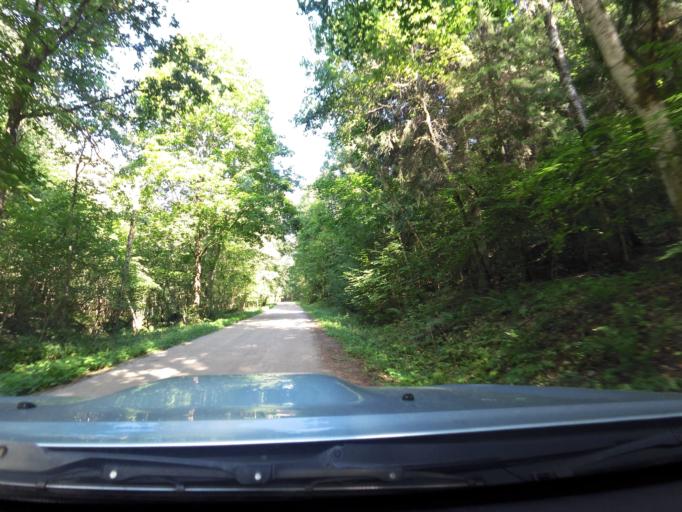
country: LT
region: Vilnius County
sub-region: Vilniaus Rajonas
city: Vievis
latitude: 54.8147
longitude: 24.9651
